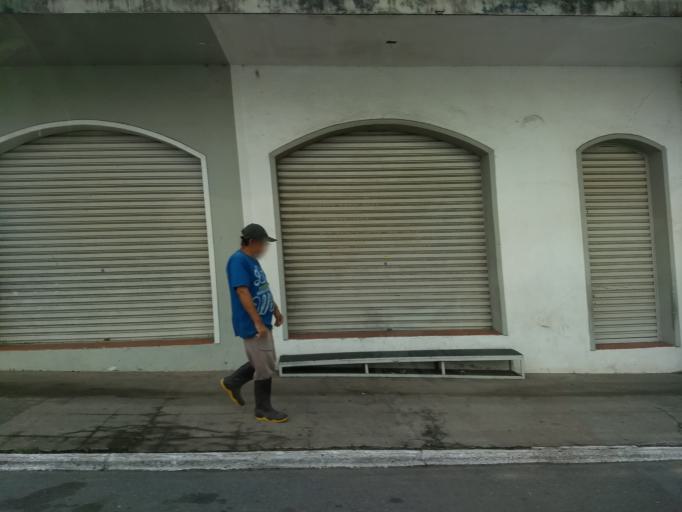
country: BR
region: Santa Catarina
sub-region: Jaragua Do Sul
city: Jaragua do Sul
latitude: -26.4842
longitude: -49.0807
